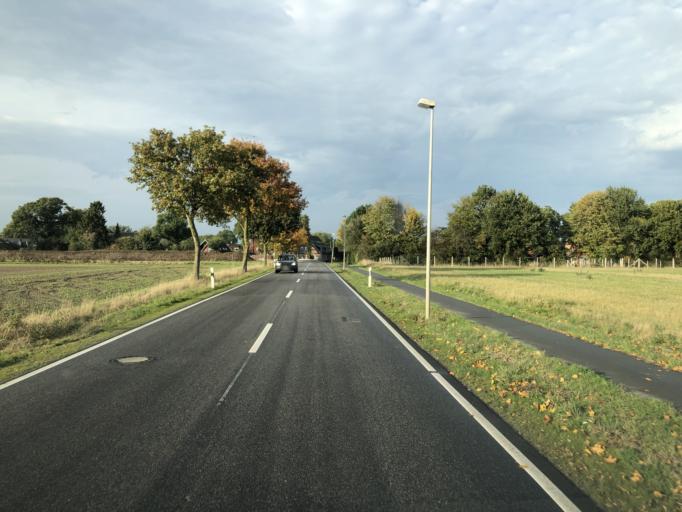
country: DE
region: Lower Saxony
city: Neu Wulmstorf
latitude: 53.4406
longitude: 9.8055
